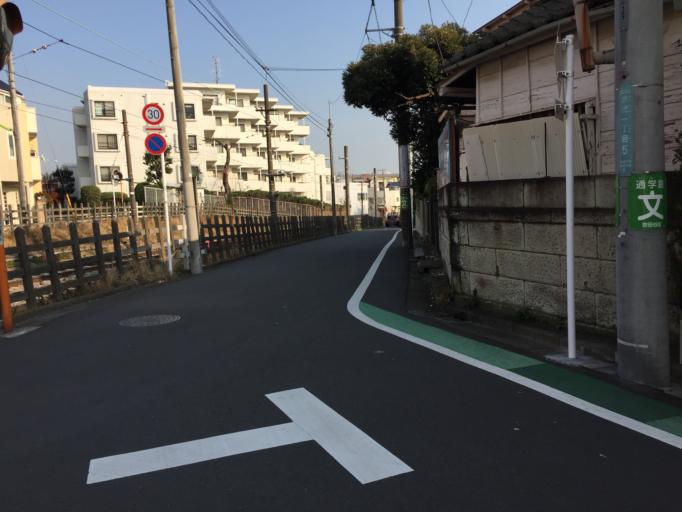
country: JP
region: Tokyo
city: Tokyo
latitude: 35.6559
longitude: 139.6451
